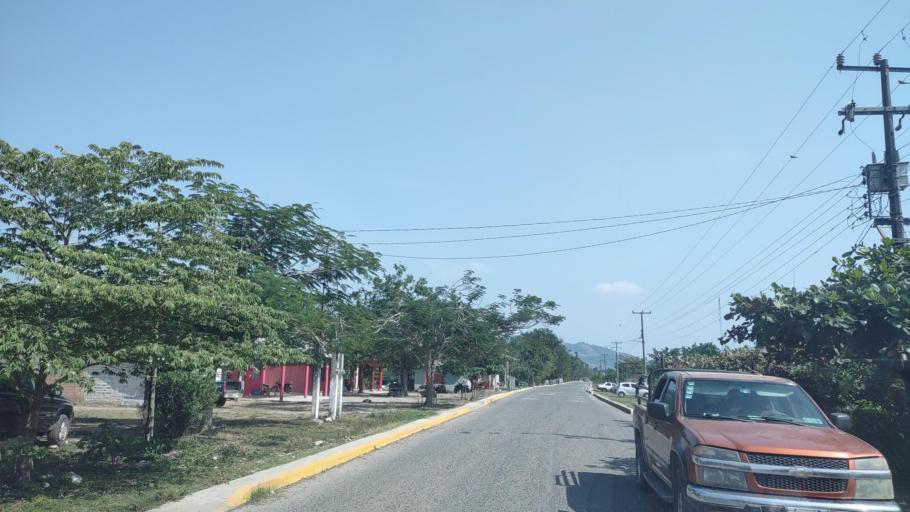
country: MX
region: Puebla
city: Espinal
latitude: 20.2625
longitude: -97.3110
